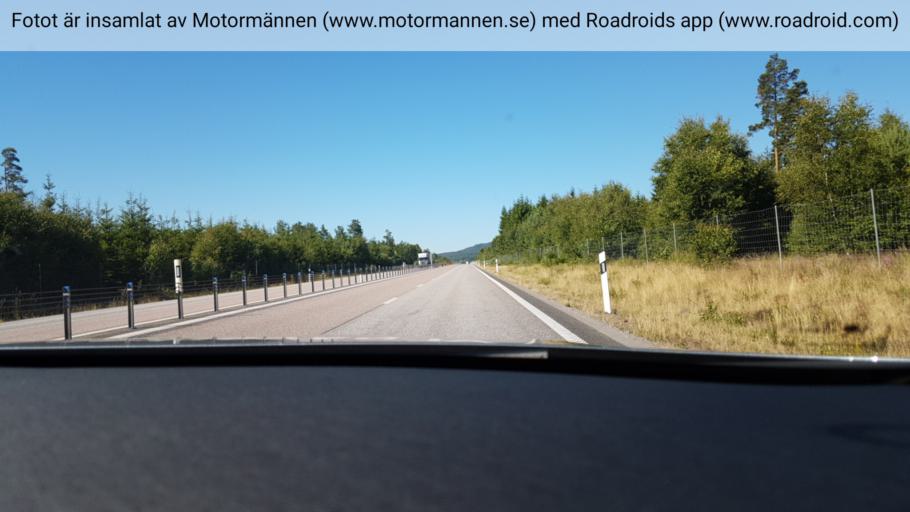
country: SE
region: Vaestra Goetaland
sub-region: Skovde Kommun
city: Skultorp
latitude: 58.3335
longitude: 13.8556
